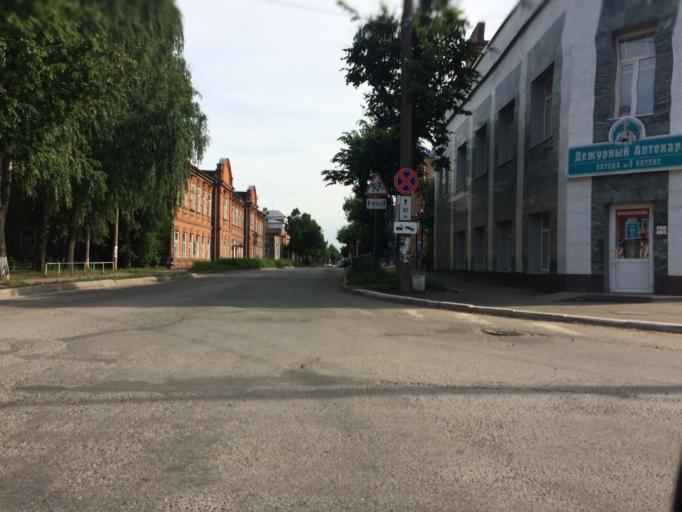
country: RU
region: Mariy-El
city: Yoshkar-Ola
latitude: 56.6395
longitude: 47.9009
